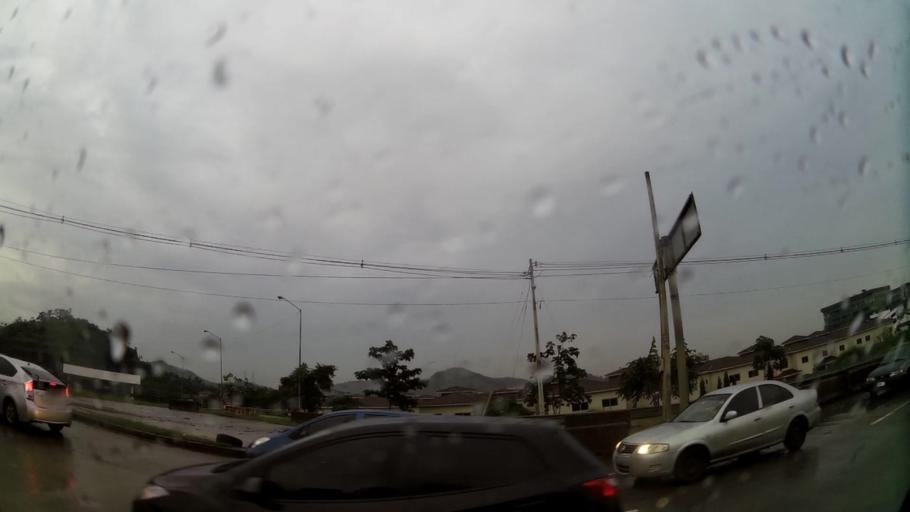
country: PA
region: Panama
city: Panama
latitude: 9.0325
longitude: -79.5354
